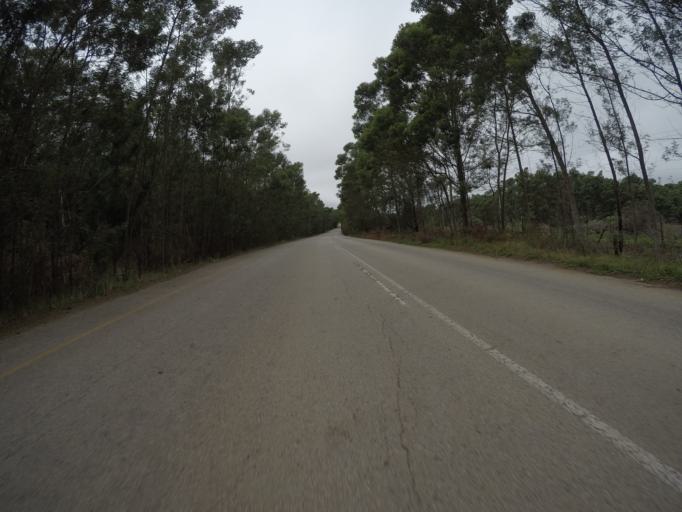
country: ZA
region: Eastern Cape
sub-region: Cacadu District Municipality
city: Kareedouw
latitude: -33.9966
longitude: 24.1584
